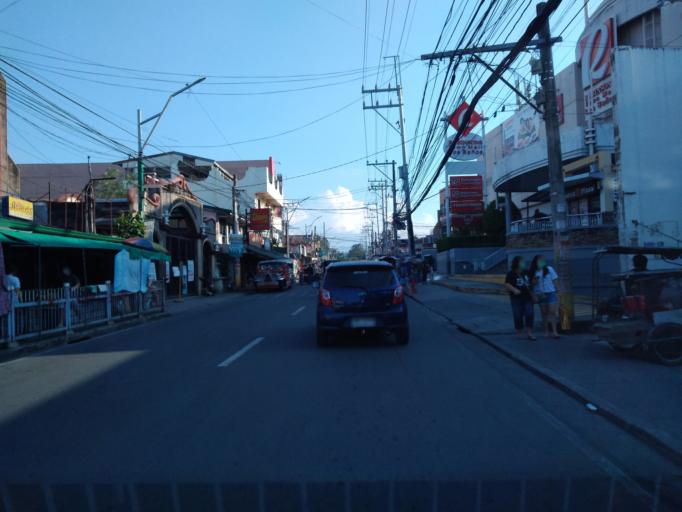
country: PH
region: Calabarzon
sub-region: Province of Laguna
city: Los Banos
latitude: 14.1776
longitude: 121.2424
